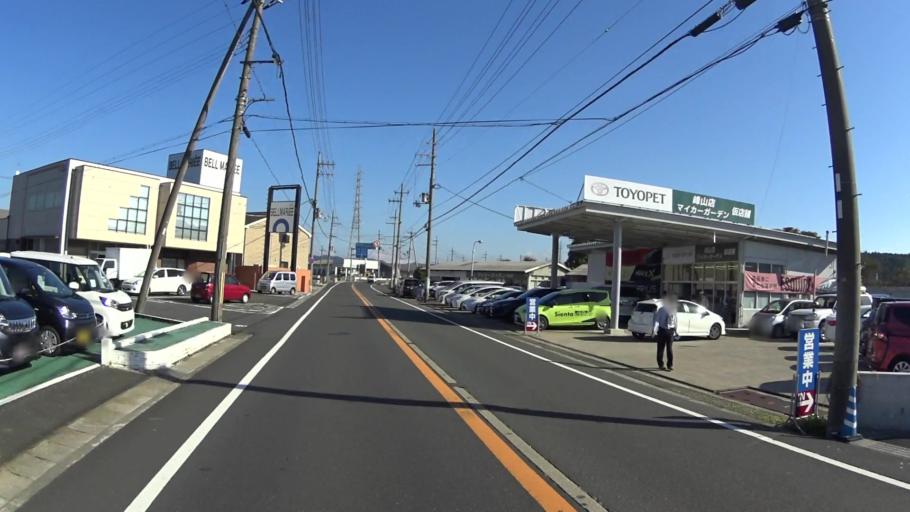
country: JP
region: Kyoto
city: Miyazu
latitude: 35.6117
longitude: 135.0665
